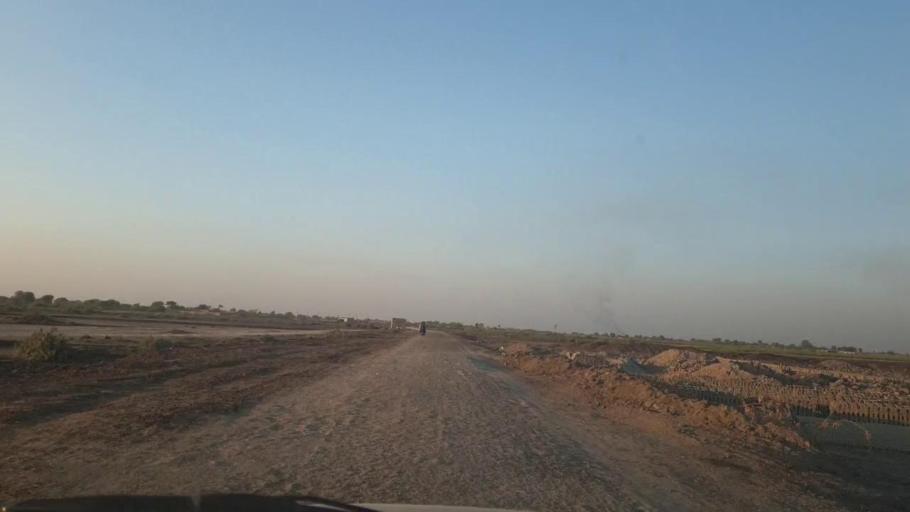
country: PK
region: Sindh
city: Mirpur Khas
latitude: 25.4600
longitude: 69.0721
